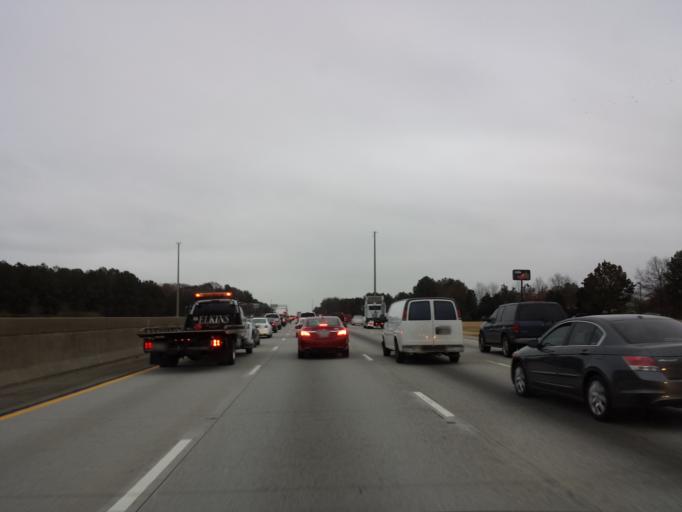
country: US
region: Georgia
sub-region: Clayton County
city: Morrow
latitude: 33.5639
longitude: -84.3187
